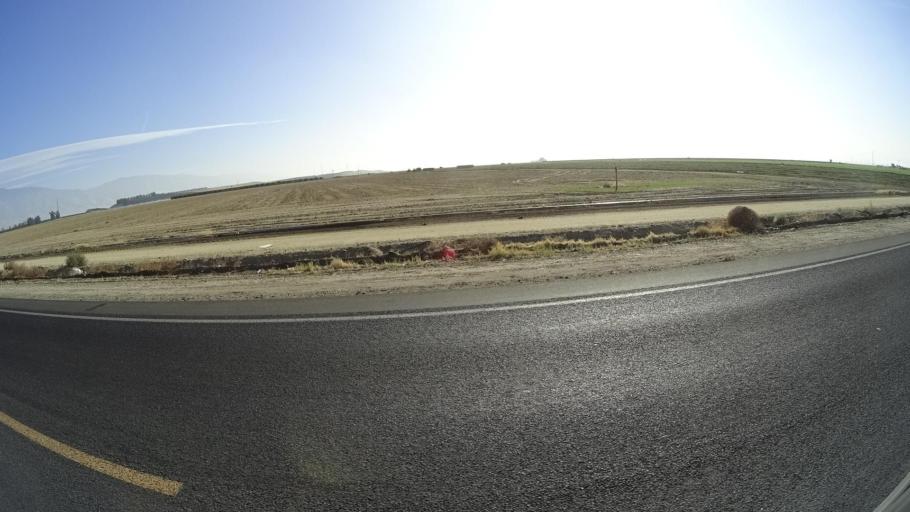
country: US
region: California
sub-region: Kern County
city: Arvin
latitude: 35.3302
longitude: -118.7986
